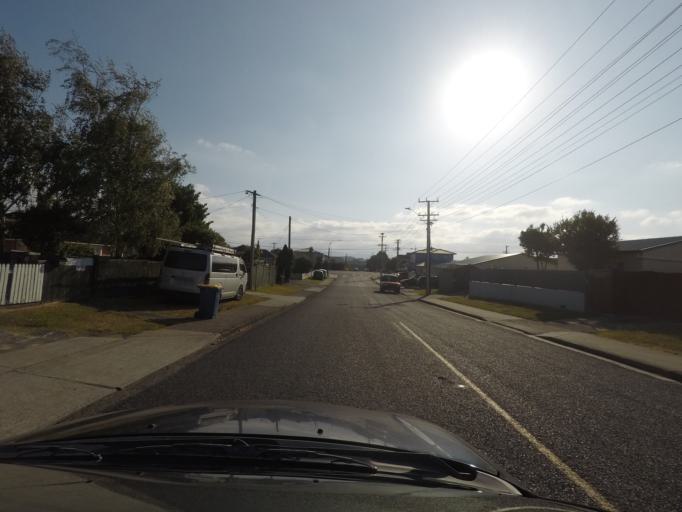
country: NZ
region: Auckland
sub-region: Auckland
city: Rosebank
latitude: -36.8568
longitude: 174.6437
